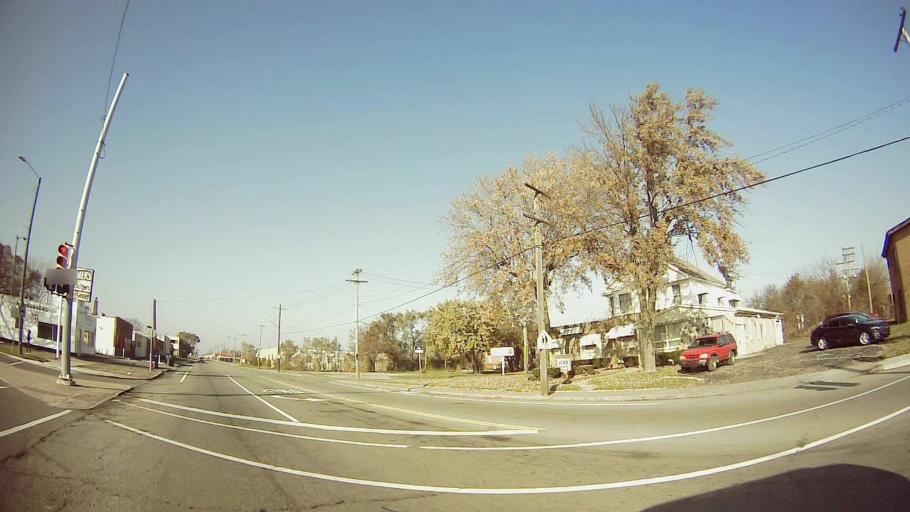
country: US
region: Michigan
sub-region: Wayne County
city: Dearborn
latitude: 42.3662
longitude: -83.1534
